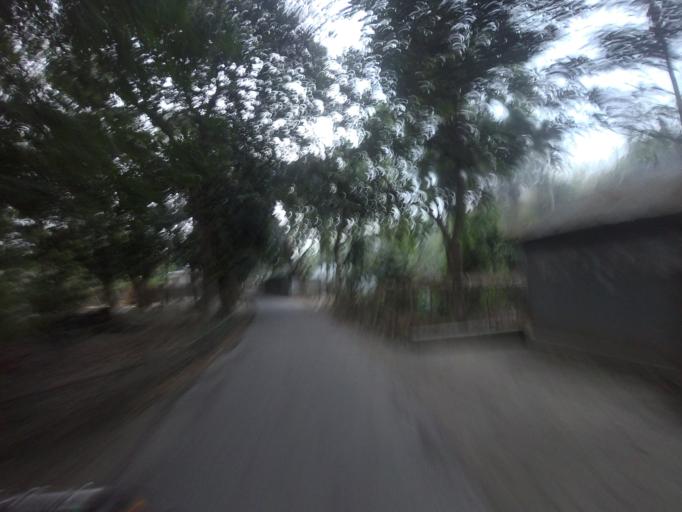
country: BD
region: Rajshahi
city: Sirajganj
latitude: 24.3176
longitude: 89.6609
